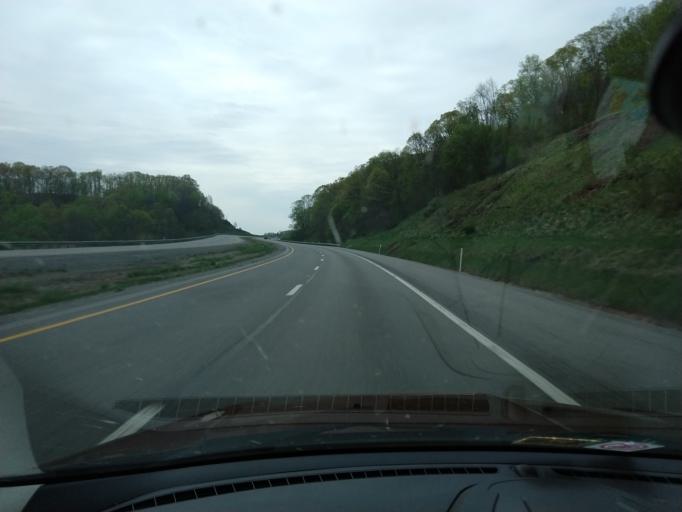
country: US
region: West Virginia
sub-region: Lewis County
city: Weston
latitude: 38.9230
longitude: -80.5489
